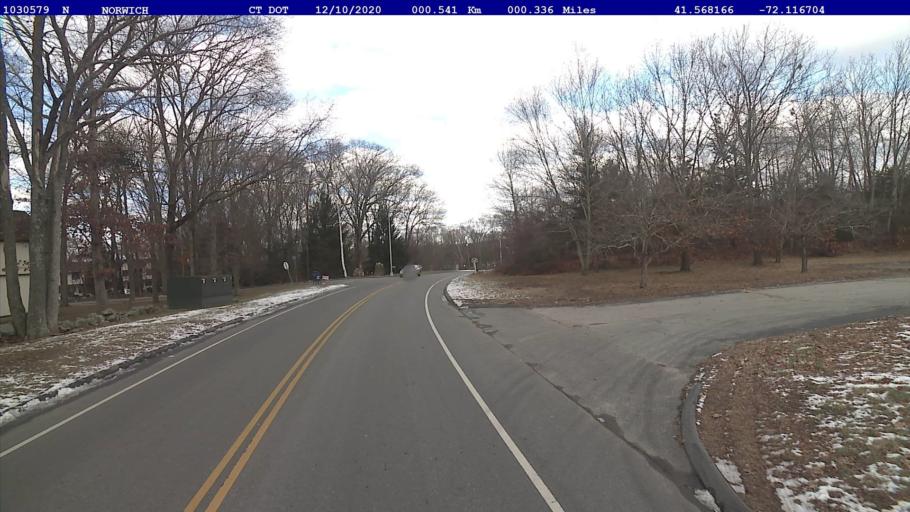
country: US
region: Connecticut
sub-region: New London County
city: Baltic
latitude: 41.5683
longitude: -72.1166
